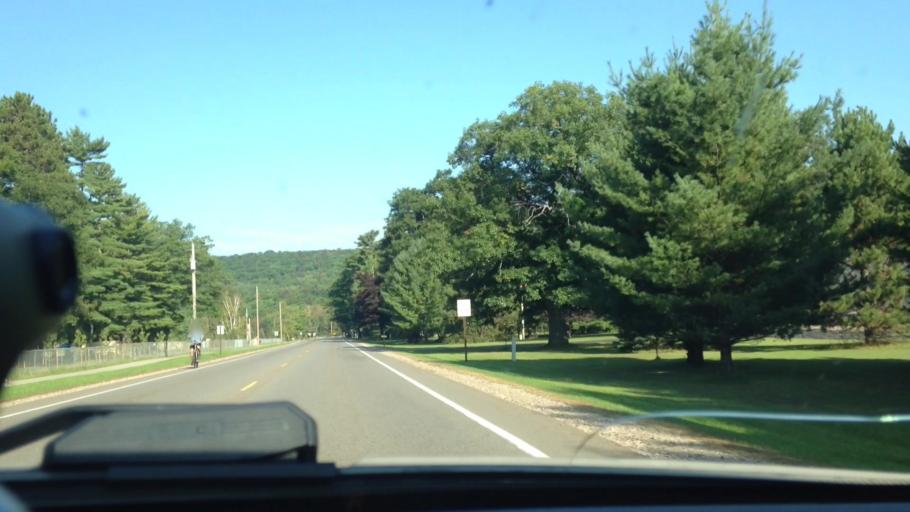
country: US
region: Michigan
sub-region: Dickinson County
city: Quinnesec
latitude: 45.8397
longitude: -88.0135
